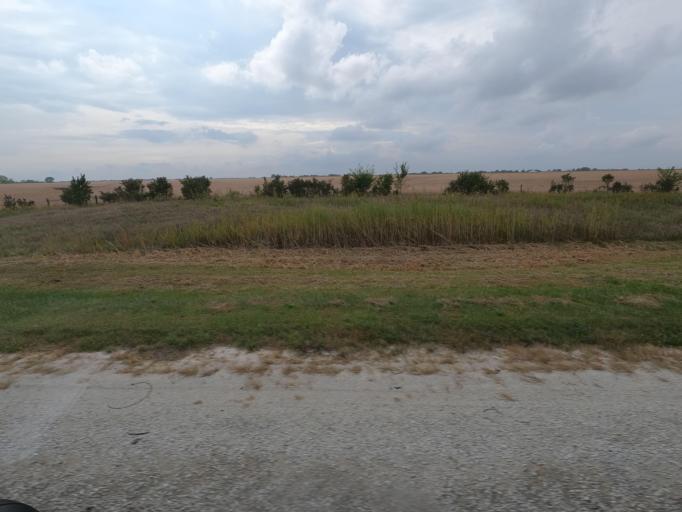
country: US
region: Iowa
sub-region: Wapello County
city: Ottumwa
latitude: 41.0862
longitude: -92.3947
